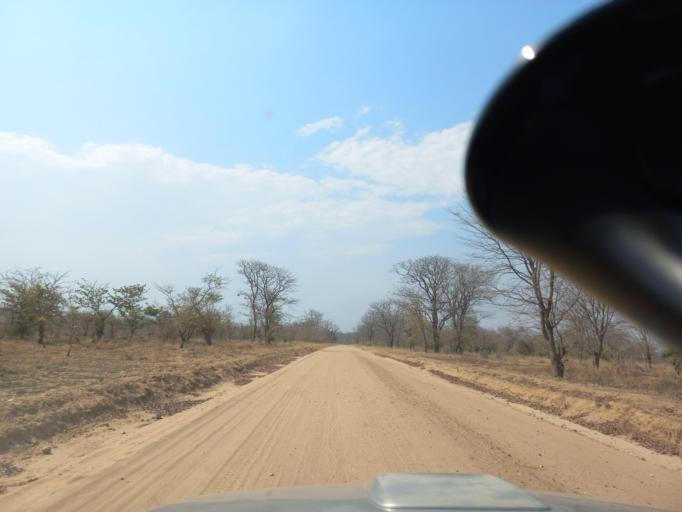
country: ZW
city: Chirundu
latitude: -15.9358
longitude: 28.9147
